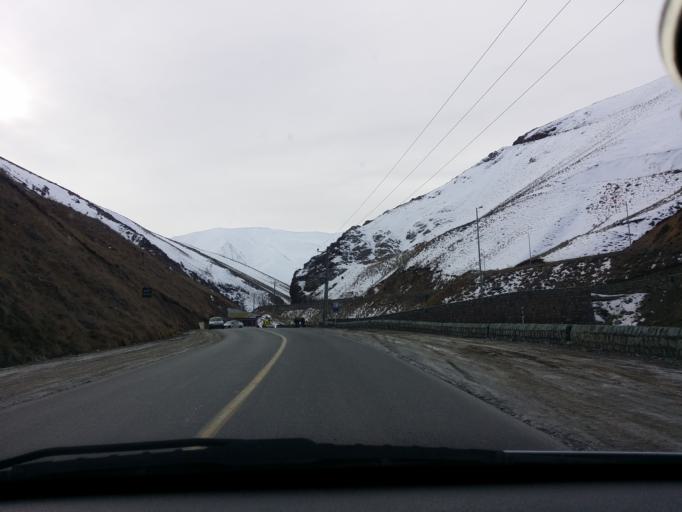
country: IR
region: Tehran
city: Tajrish
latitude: 36.1734
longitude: 51.3152
